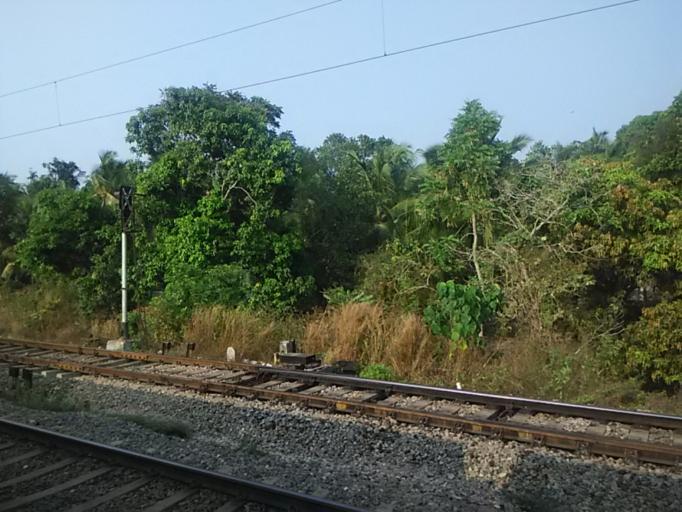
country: IN
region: Kerala
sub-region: Malappuram
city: Pariyapuram
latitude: 11.0426
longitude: 75.8625
